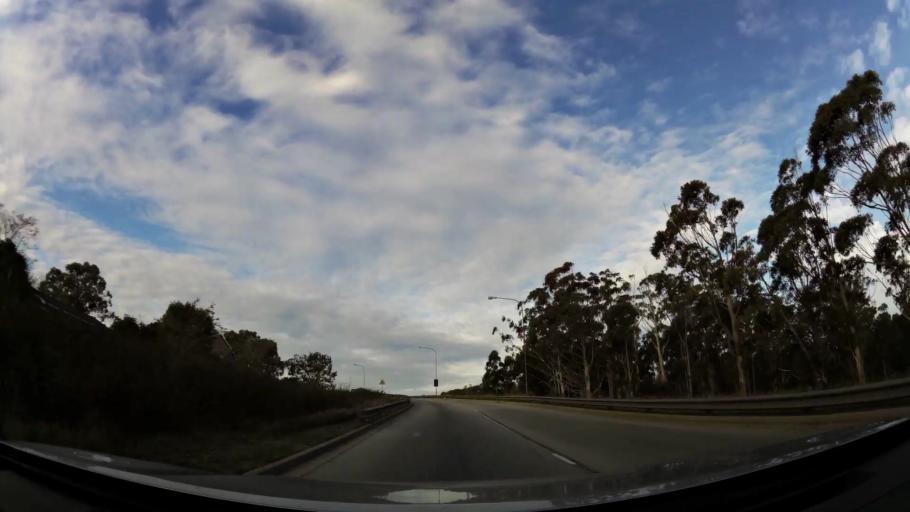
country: ZA
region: Eastern Cape
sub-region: Nelson Mandela Bay Metropolitan Municipality
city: Port Elizabeth
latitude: -33.9530
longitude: 25.5109
